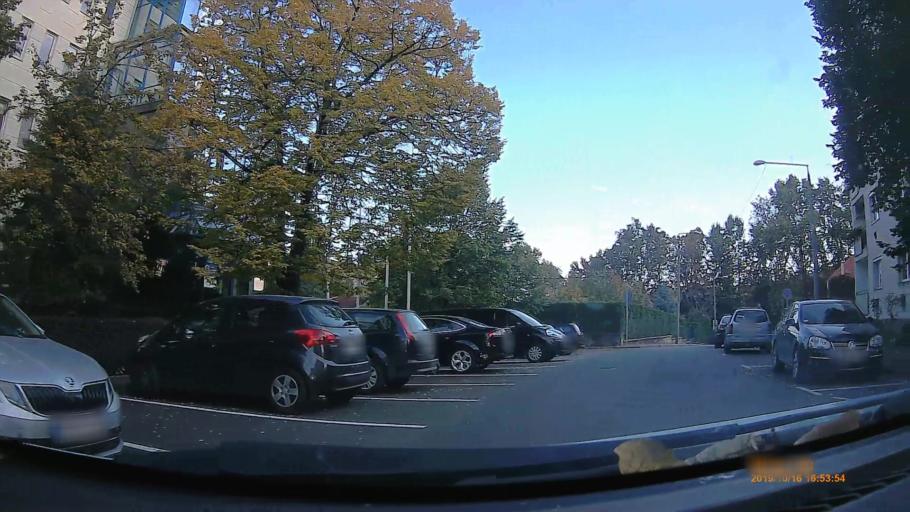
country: HU
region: Heves
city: Eger
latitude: 47.8955
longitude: 20.3776
